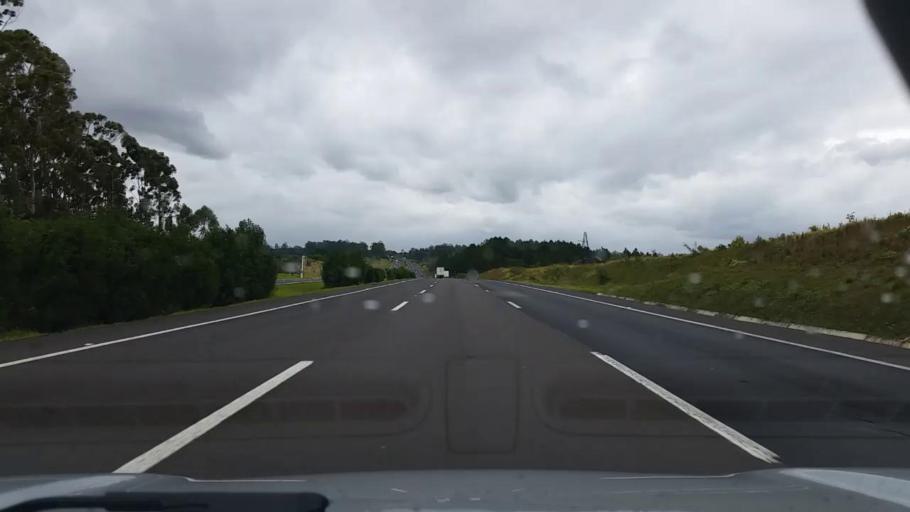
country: BR
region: Rio Grande do Sul
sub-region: Gravatai
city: Gravatai
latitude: -29.9248
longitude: -50.8593
